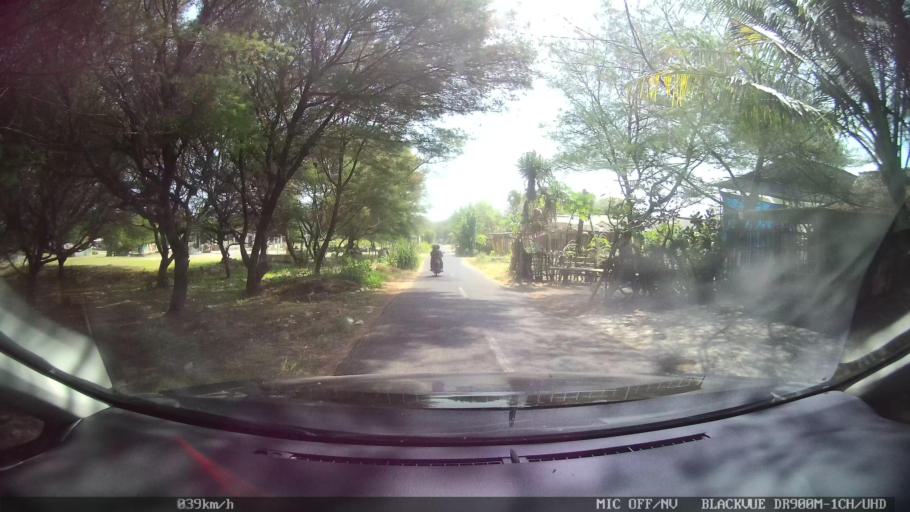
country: ID
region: Daerah Istimewa Yogyakarta
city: Bambanglipuro
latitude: -8.0173
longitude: 110.3094
